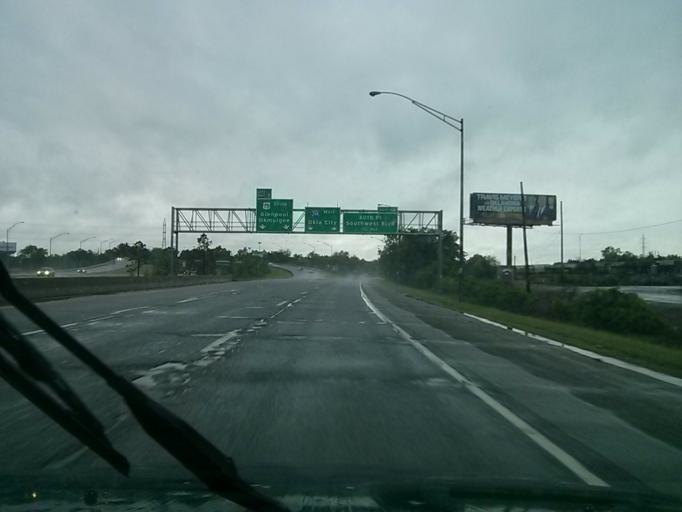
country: US
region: Oklahoma
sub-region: Tulsa County
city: Tulsa
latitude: 36.1150
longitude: -96.0110
